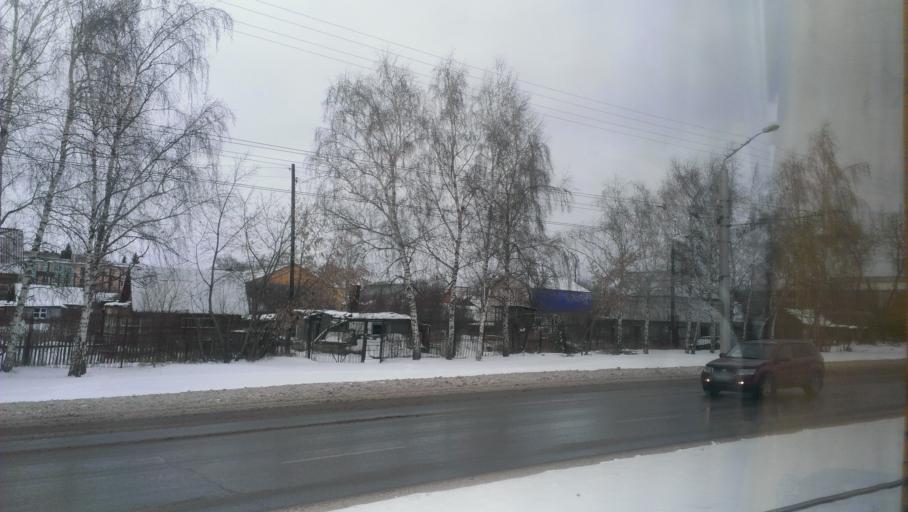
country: RU
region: Altai Krai
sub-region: Gorod Barnaulskiy
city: Barnaul
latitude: 53.3811
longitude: 83.7131
